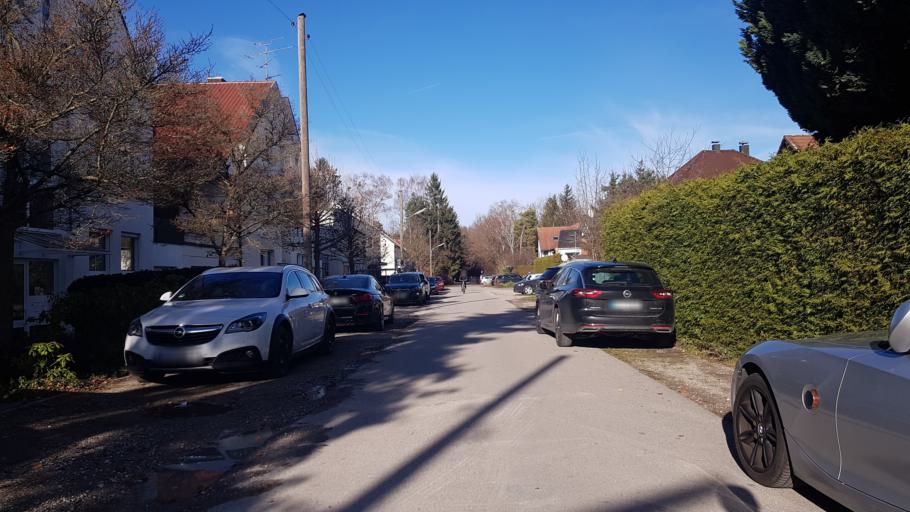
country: DE
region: Bavaria
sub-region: Upper Bavaria
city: Karlsfeld
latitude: 48.1889
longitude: 11.5125
